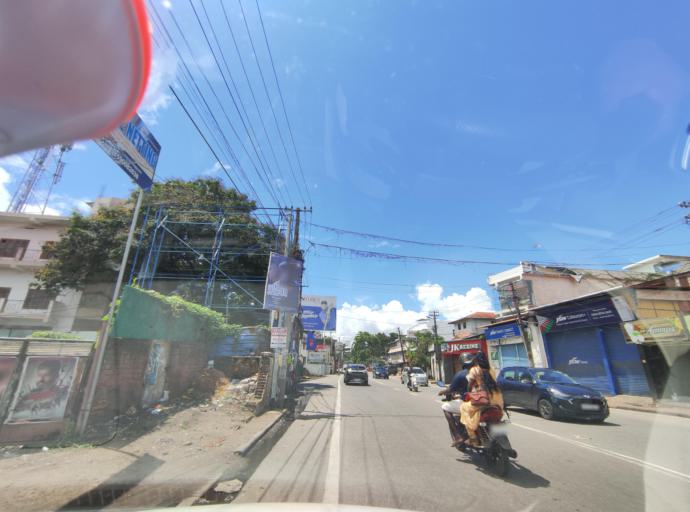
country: IN
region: Kerala
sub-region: Thiruvananthapuram
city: Thiruvananthapuram
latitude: 8.4845
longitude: 76.9555
